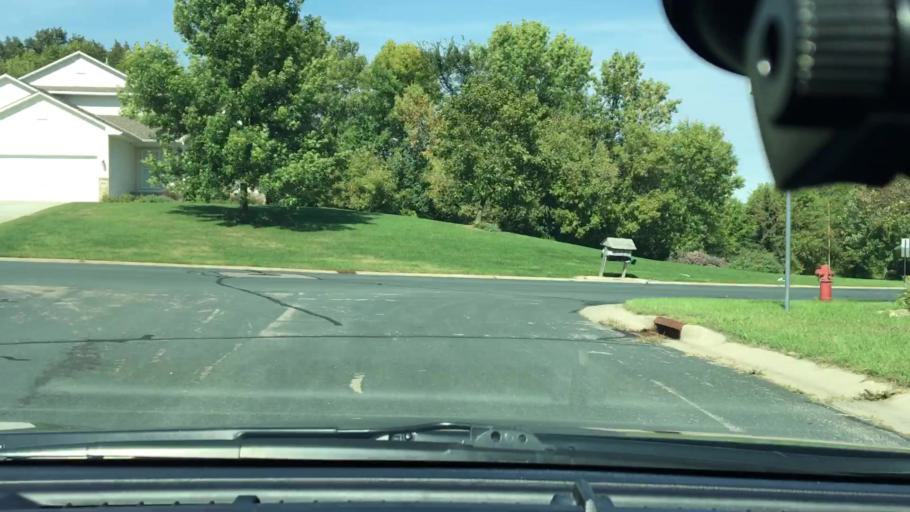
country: US
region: Minnesota
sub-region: Wright County
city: Hanover
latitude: 45.1635
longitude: -93.6777
